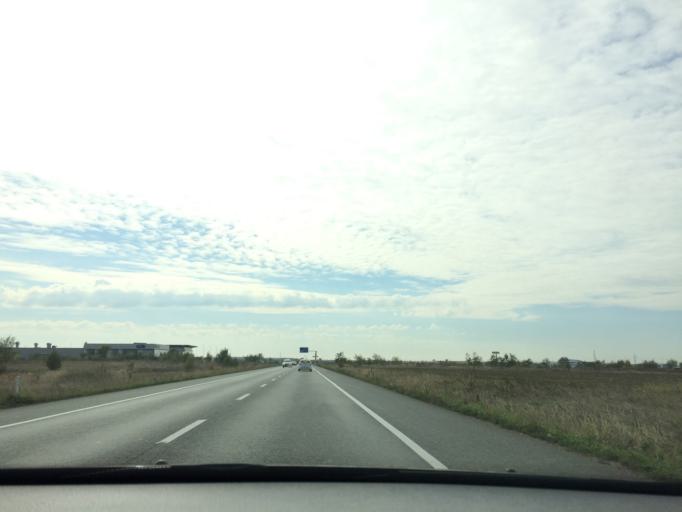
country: RO
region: Timis
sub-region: Comuna Ghiroda
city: Giarmata-Vii
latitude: 45.7924
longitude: 21.3138
